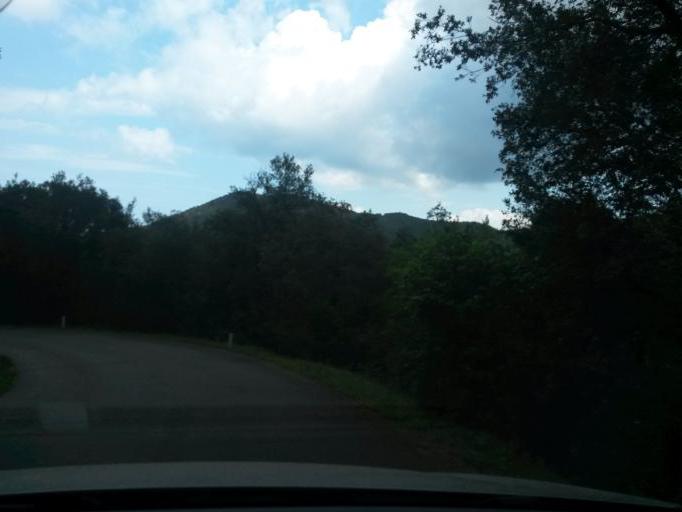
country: IT
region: Tuscany
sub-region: Provincia di Livorno
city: Rio nell'Elba
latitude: 42.8295
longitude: 10.3865
